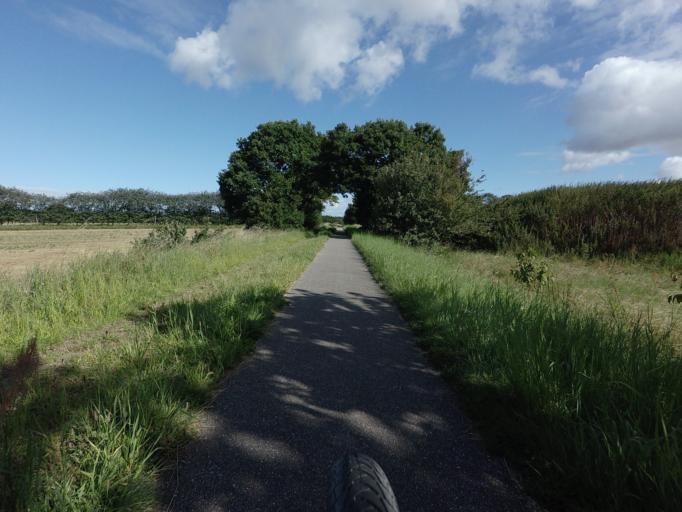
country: DK
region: Central Jutland
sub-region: Horsens Kommune
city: Horsens
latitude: 55.9163
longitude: 9.7688
